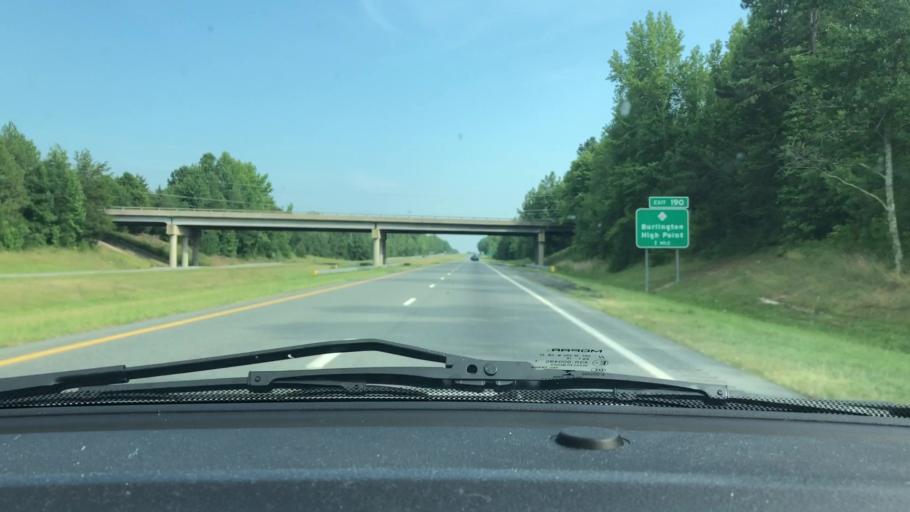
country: US
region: North Carolina
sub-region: Guilford County
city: Forest Oaks
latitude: 35.9354
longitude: -79.6844
